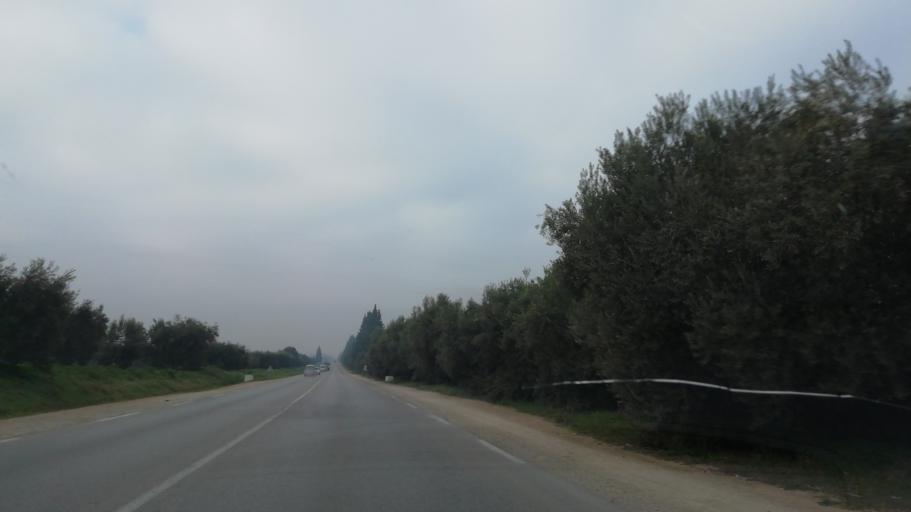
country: DZ
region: Relizane
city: Oued Rhiou
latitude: 35.9484
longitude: 0.8754
